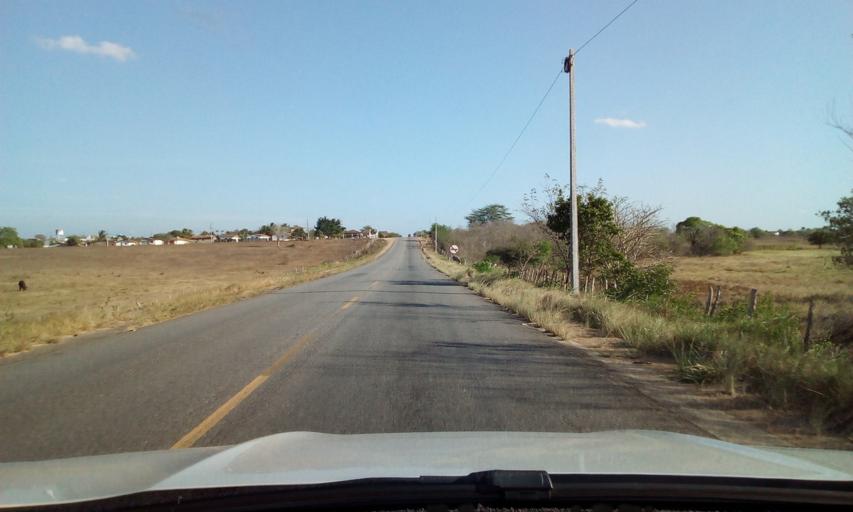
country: BR
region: Paraiba
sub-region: Mulungu
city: Mulungu
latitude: -6.9559
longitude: -35.4156
